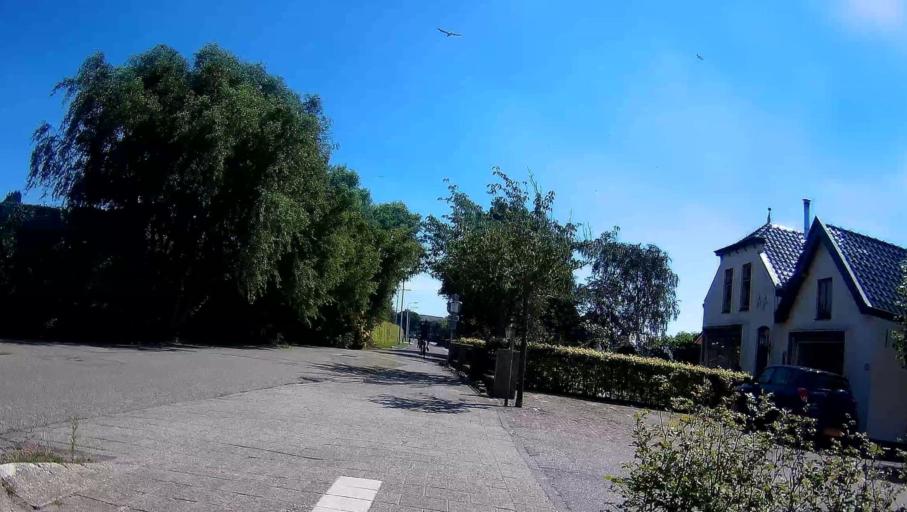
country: NL
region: South Holland
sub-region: Gemeente Westland
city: Naaldwijk
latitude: 52.0015
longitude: 4.1887
